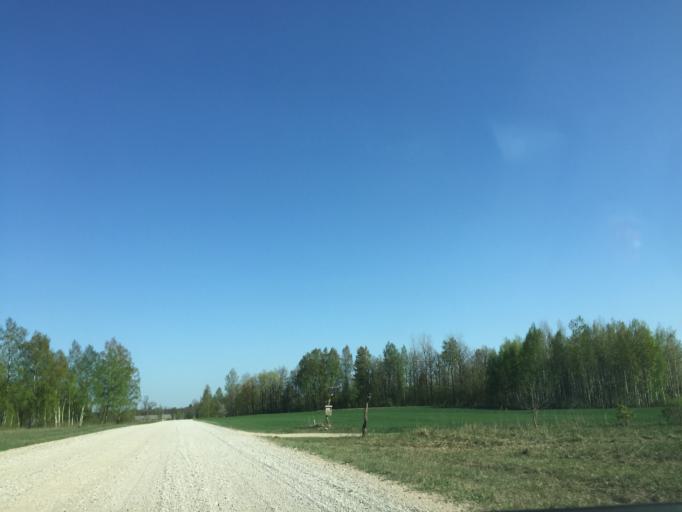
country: LV
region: Skriveri
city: Skriveri
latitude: 56.8366
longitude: 25.1159
